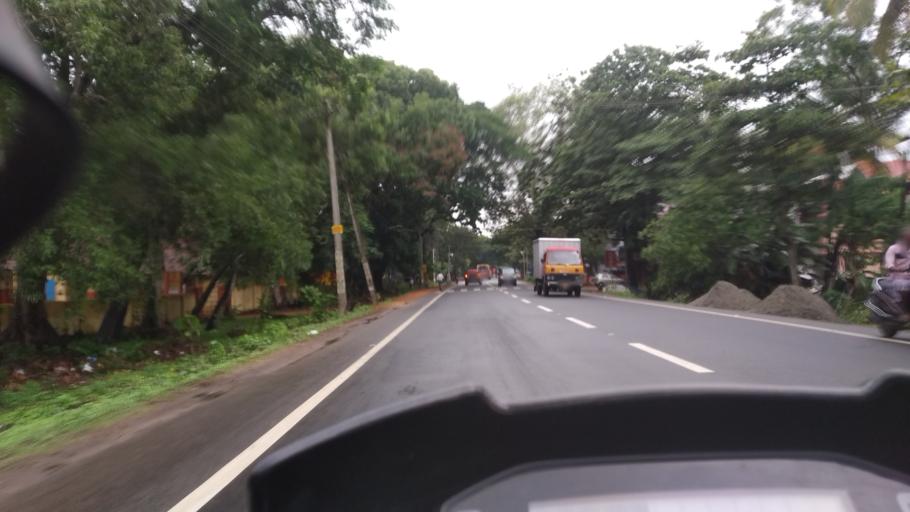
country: IN
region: Kerala
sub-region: Alappuzha
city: Mavelikara
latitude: 9.3000
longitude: 76.4334
